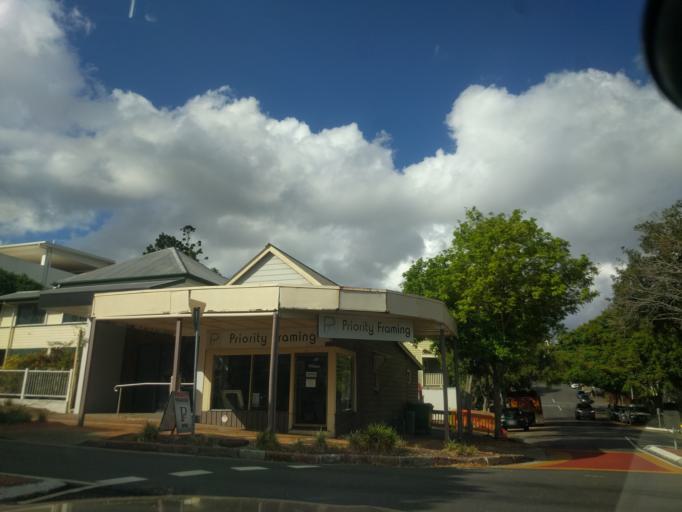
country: AU
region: Queensland
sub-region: Brisbane
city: Fortitude Valley
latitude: -27.4621
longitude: 153.0467
